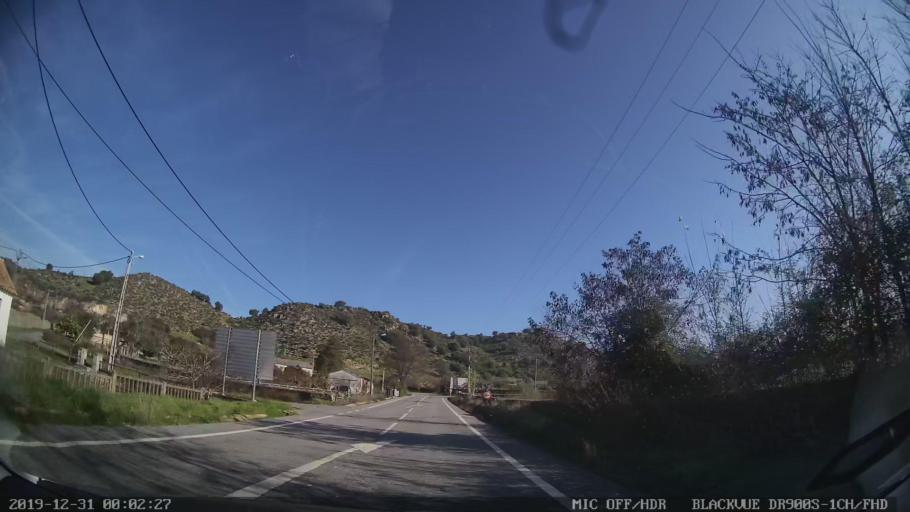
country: PT
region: Castelo Branco
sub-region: Idanha-A-Nova
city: Idanha-a-Nova
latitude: 39.9166
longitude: -7.2230
